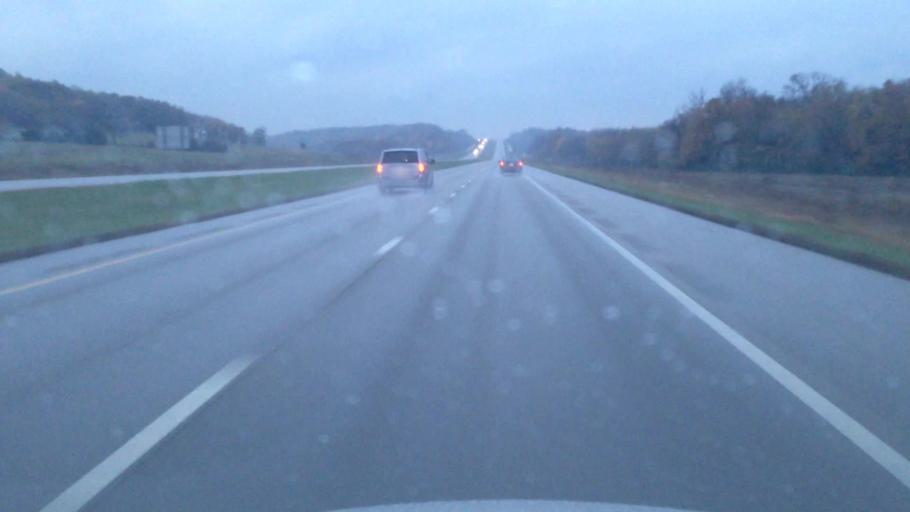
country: US
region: Kansas
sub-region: Douglas County
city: Lawrence
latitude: 38.8658
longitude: -95.2579
